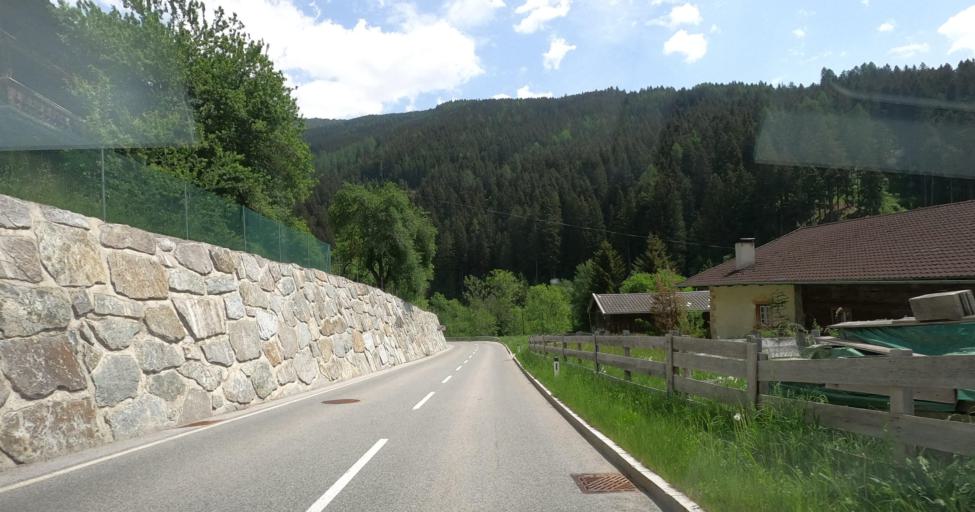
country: AT
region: Tyrol
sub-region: Politischer Bezirk Innsbruck Land
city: Ellbogen
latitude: 47.1631
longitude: 11.4572
